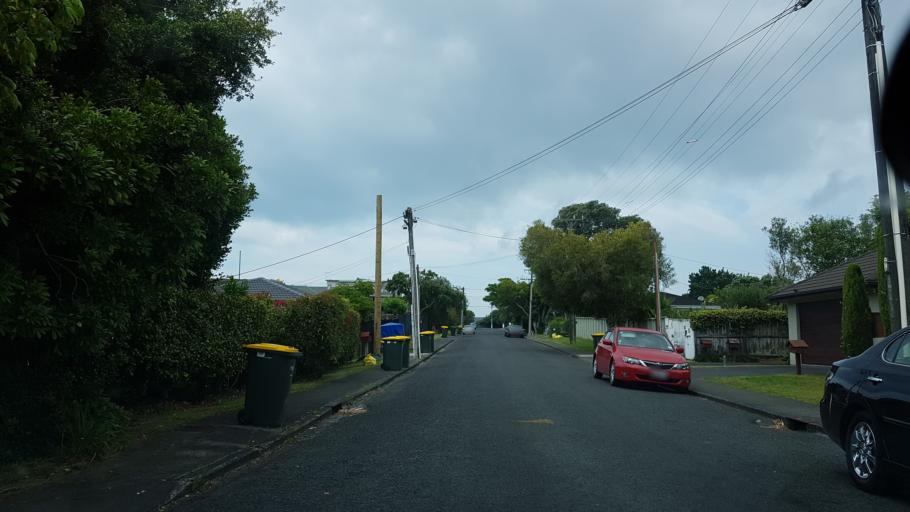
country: NZ
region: Auckland
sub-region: Auckland
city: North Shore
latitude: -36.8012
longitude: 174.7731
